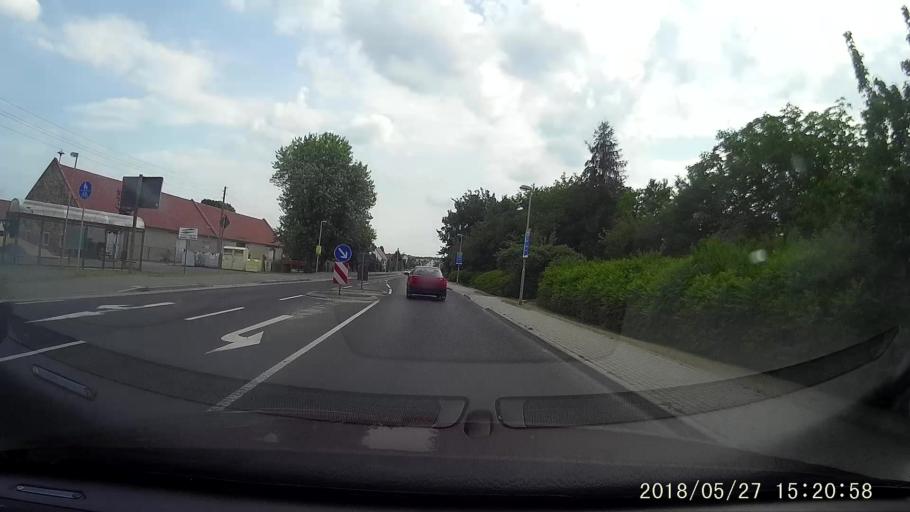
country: DE
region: Saxony
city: Kodersdorf
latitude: 51.2441
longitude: 14.8889
